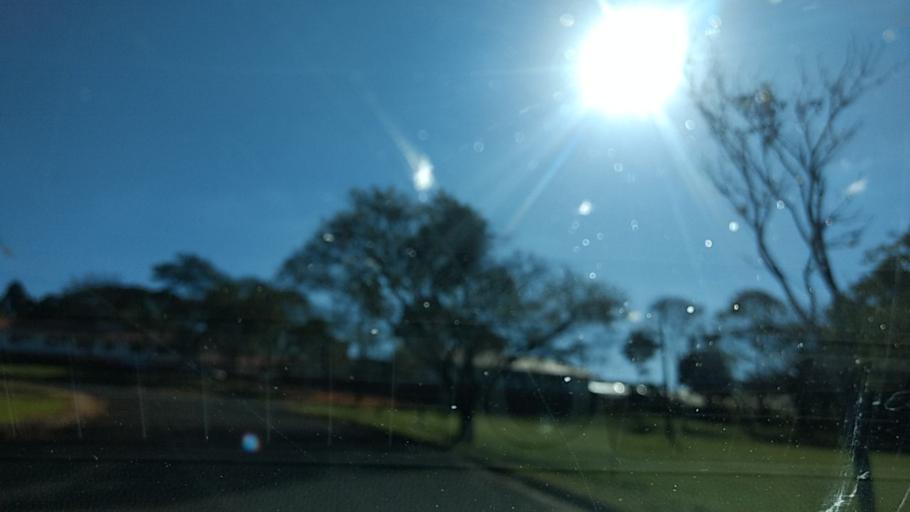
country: BR
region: Sao Paulo
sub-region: Botucatu
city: Botucatu
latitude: -22.8459
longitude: -48.4337
